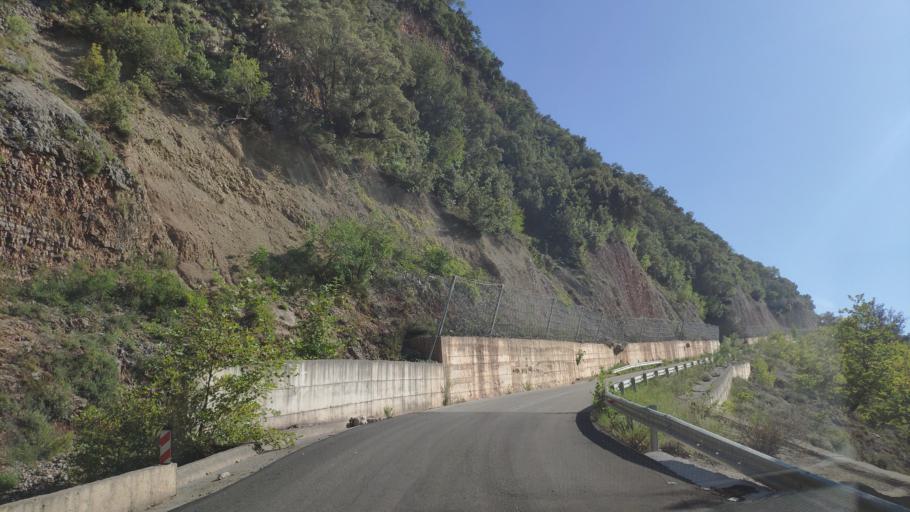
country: GR
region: Central Greece
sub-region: Nomos Evrytanias
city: Kerasochori
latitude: 39.0201
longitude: 21.6014
